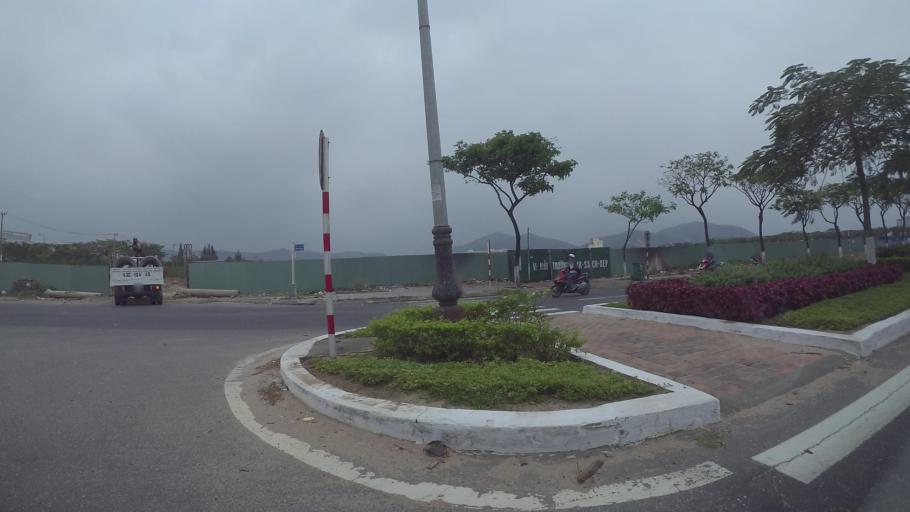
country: VN
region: Da Nang
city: Lien Chieu
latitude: 16.0722
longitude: 108.1632
